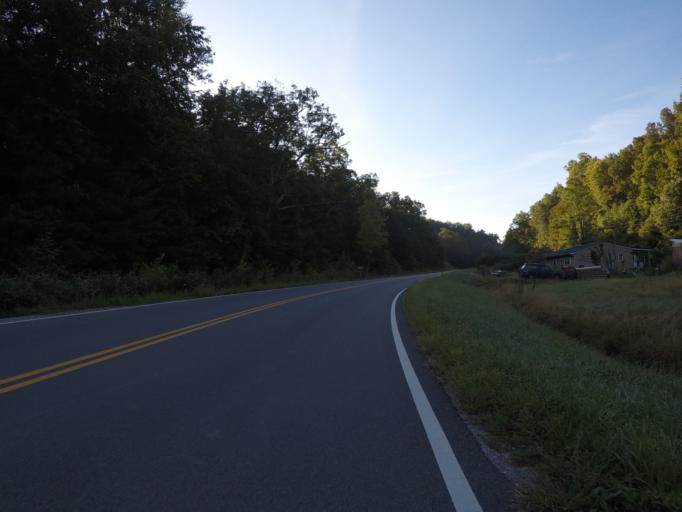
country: US
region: Ohio
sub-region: Lawrence County
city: Coal Grove
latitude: 38.6055
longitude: -82.5715
